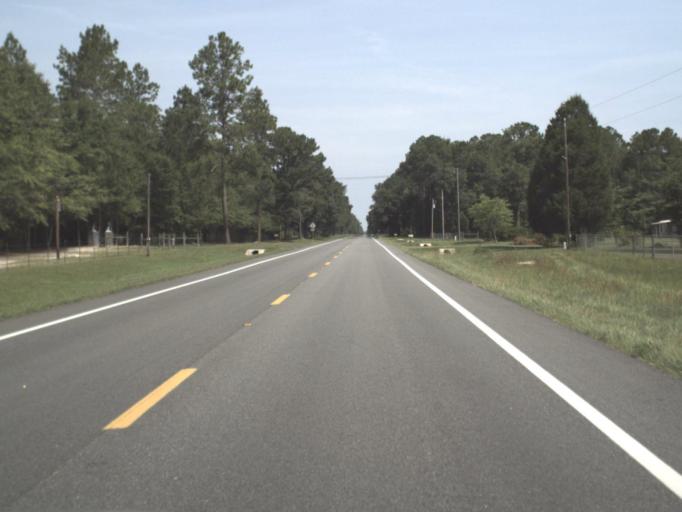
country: US
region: Florida
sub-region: Hamilton County
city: Jasper
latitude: 30.5703
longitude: -82.9909
